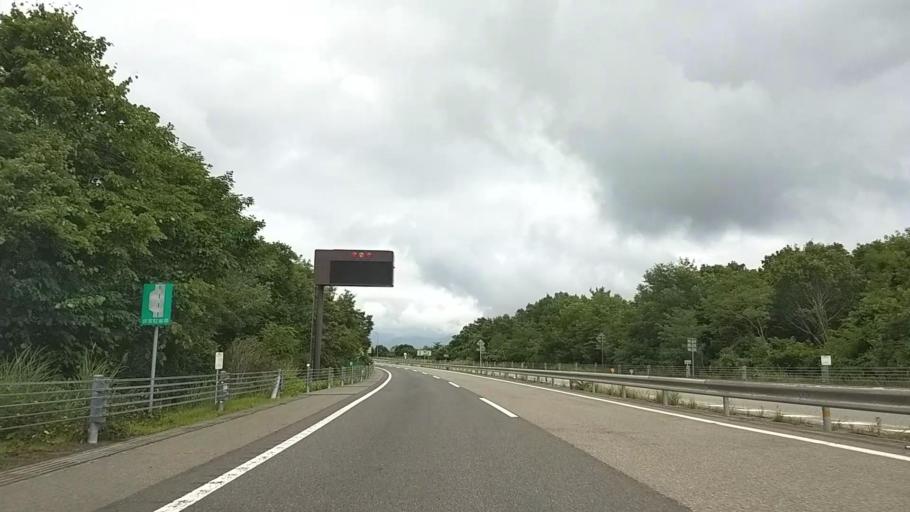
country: JP
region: Shizuoka
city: Gotemba
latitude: 35.4284
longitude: 138.8398
